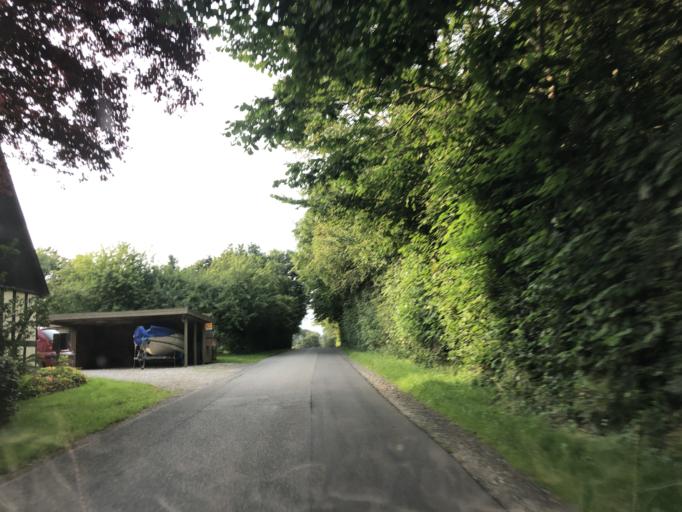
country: DK
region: South Denmark
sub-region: Fredericia Kommune
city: Taulov
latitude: 55.6006
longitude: 9.6019
